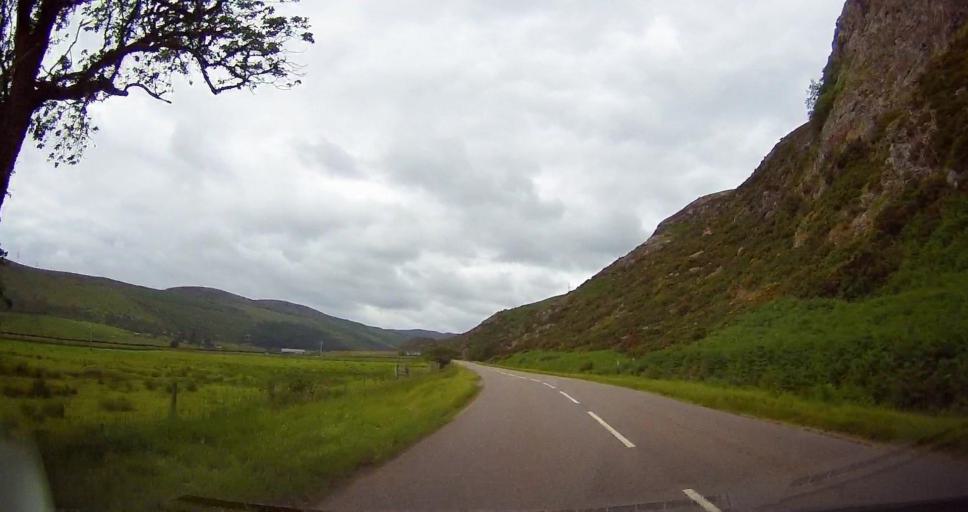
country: GB
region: Scotland
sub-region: Highland
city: Dornoch
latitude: 57.9817
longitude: -4.1181
